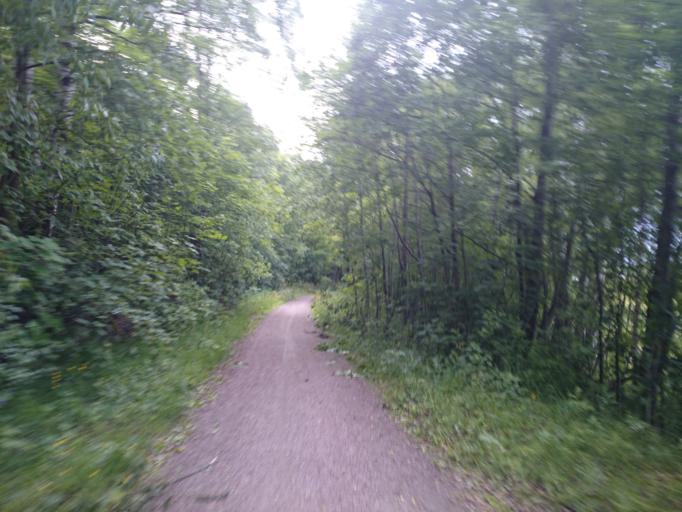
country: SE
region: Vaesternorrland
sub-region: Sundsvalls Kommun
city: Stockvik
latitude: 62.3285
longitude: 17.3707
